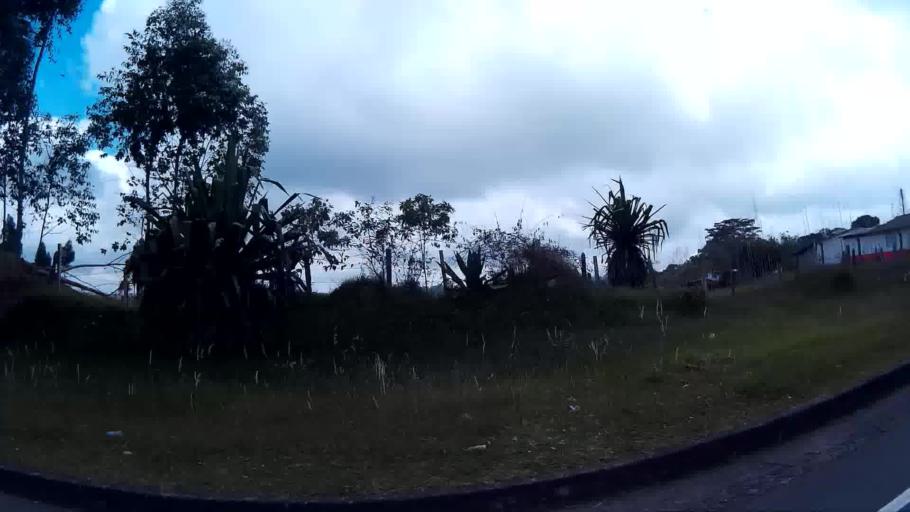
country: CO
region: Quindio
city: Circasia
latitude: 4.6439
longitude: -75.6088
